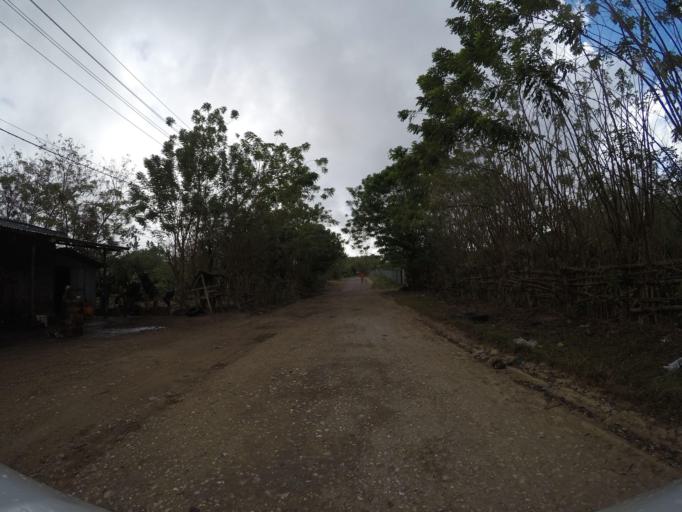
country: TL
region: Lautem
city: Lospalos
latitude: -8.5266
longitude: 126.9865
